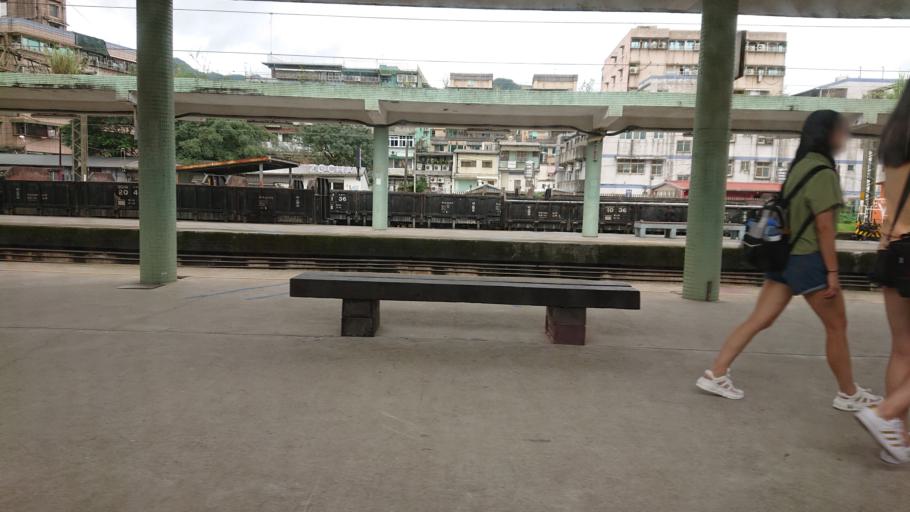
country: TW
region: Taiwan
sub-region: Keelung
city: Keelung
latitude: 25.1089
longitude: 121.8069
